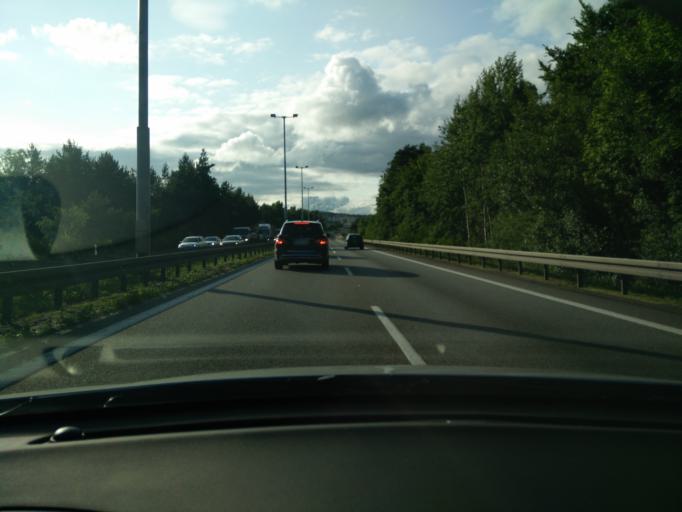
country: PL
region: Pomeranian Voivodeship
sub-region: Gdynia
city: Wielki Kack
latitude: 54.4681
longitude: 18.4775
